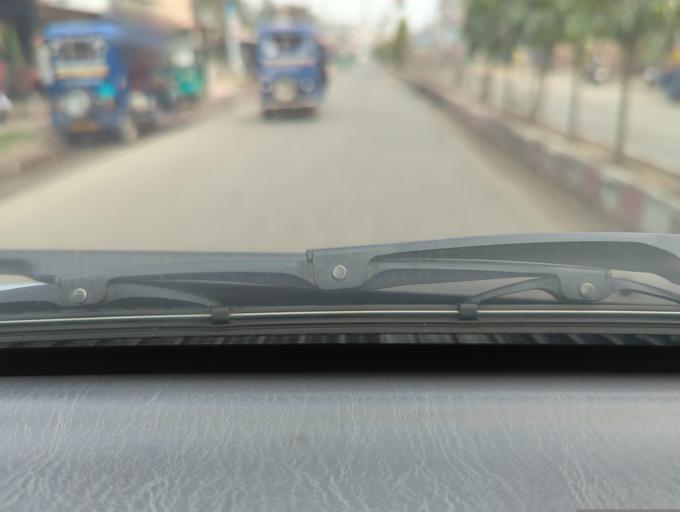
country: BD
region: Sylhet
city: Maulavi Bazar
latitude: 24.4892
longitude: 91.7519
